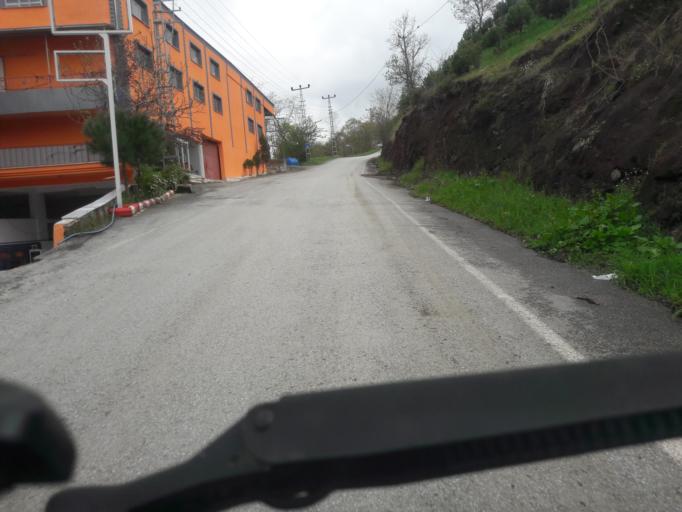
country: TR
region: Trabzon
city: Derecik
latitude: 40.9448
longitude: 39.4972
